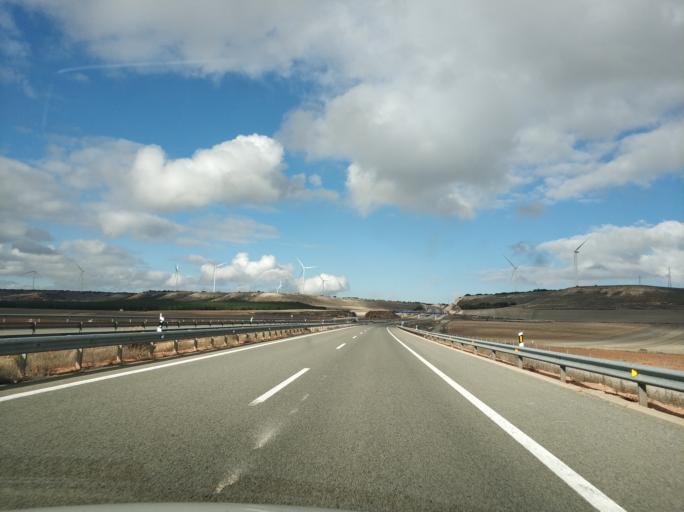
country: ES
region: Castille and Leon
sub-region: Provincia de Soria
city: Alcubilla de las Penas
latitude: 41.2796
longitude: -2.4753
